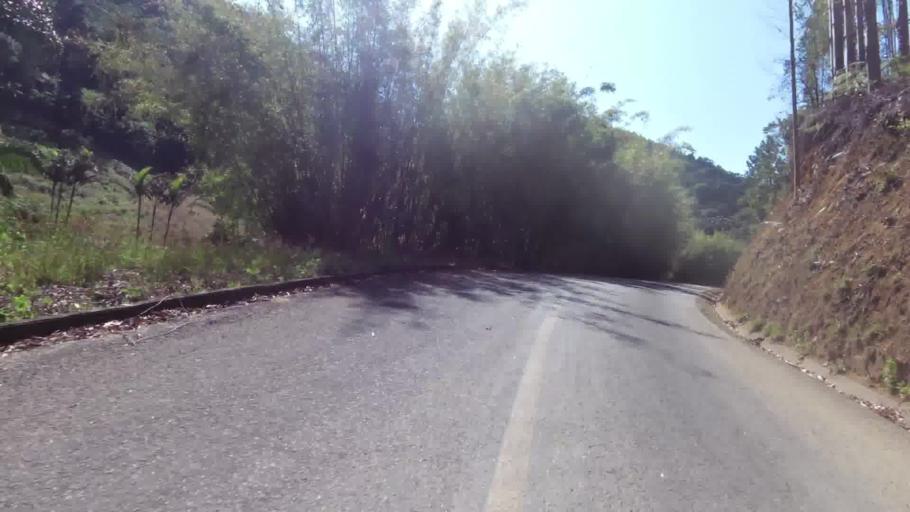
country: BR
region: Espirito Santo
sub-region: Vargem Alta
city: Vargem Alta
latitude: -20.4560
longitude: -40.9188
